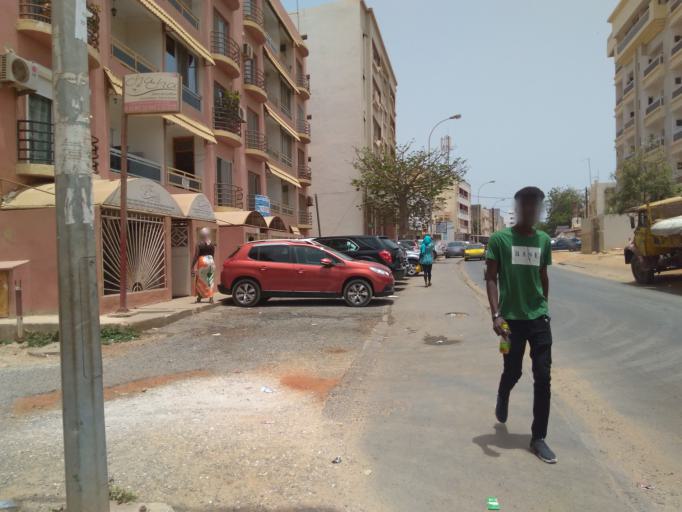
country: SN
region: Dakar
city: Grand Dakar
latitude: 14.7294
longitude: -17.4634
